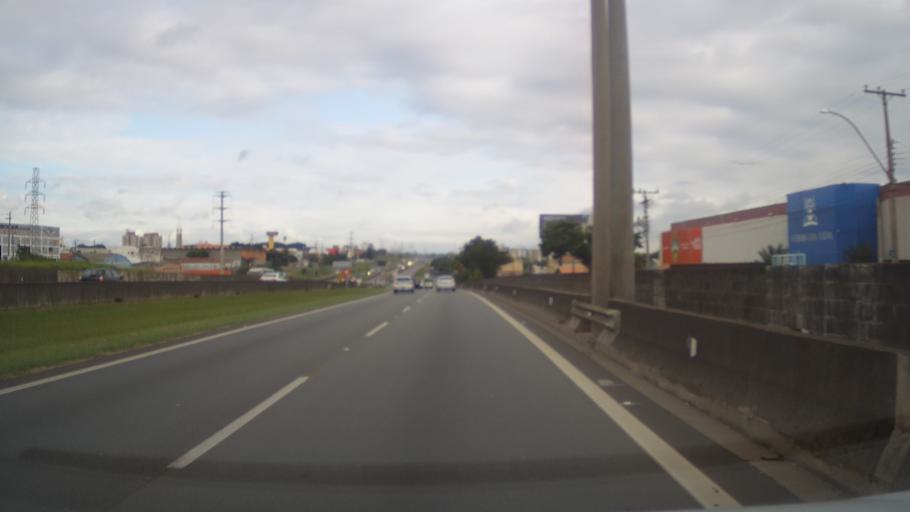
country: BR
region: Sao Paulo
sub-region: Campinas
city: Campinas
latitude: -22.9221
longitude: -47.0908
